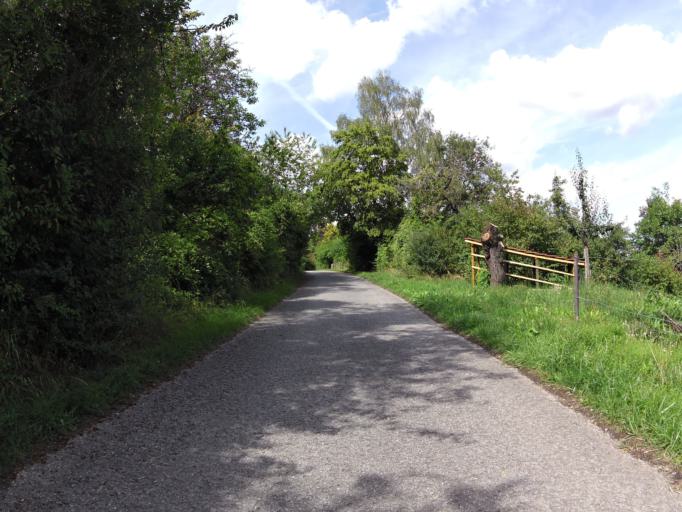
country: DE
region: Bavaria
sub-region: Regierungsbezirk Unterfranken
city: Erlabrunn
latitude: 49.8475
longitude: 9.8462
